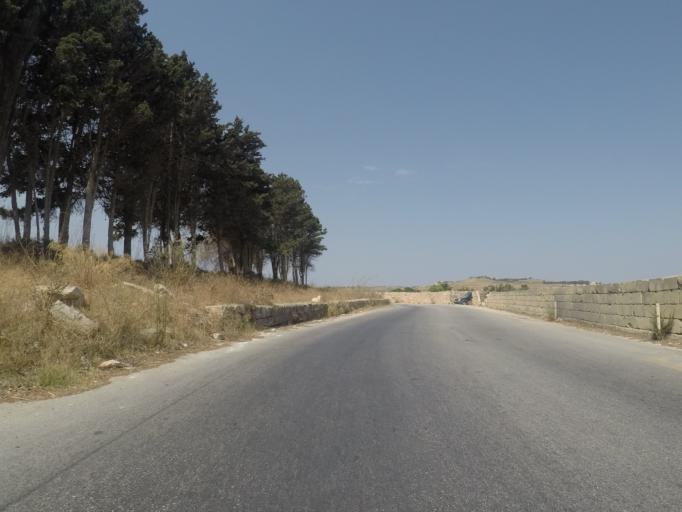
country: MT
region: Il-Mosta
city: Mosta
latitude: 35.9011
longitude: 14.4146
